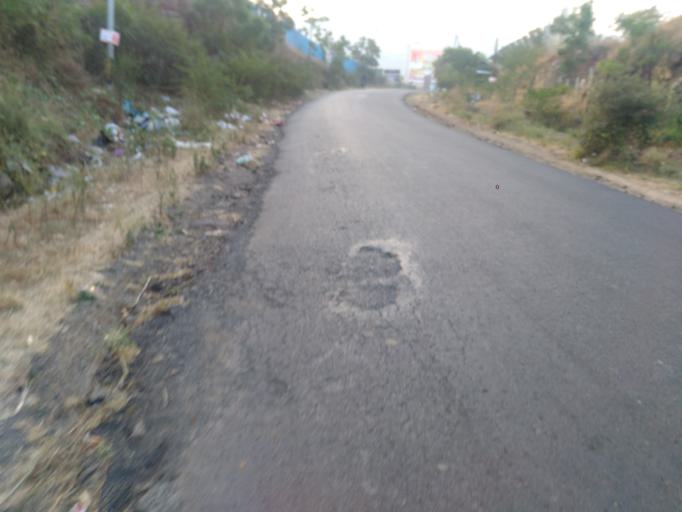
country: IN
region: Maharashtra
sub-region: Pune Division
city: Khed
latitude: 18.4258
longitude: 73.9016
